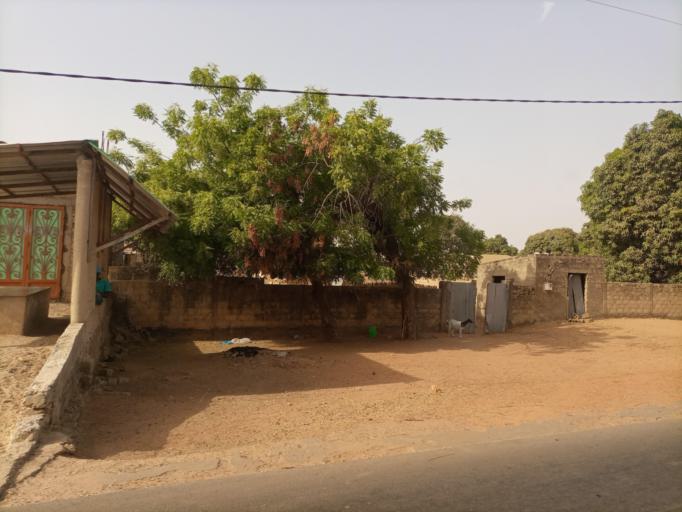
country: SN
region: Fatick
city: Foundiougne
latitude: 14.1215
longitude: -16.4333
